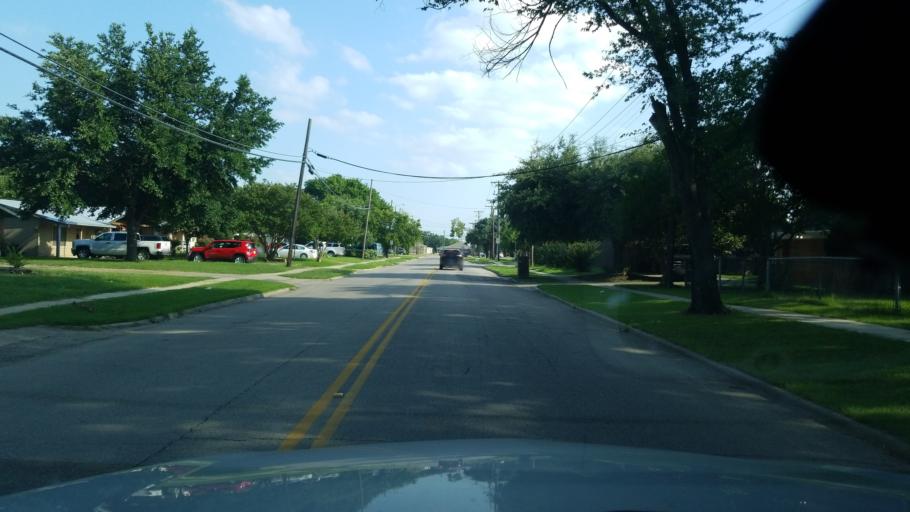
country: US
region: Texas
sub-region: Dallas County
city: Irving
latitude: 32.8245
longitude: -96.9640
